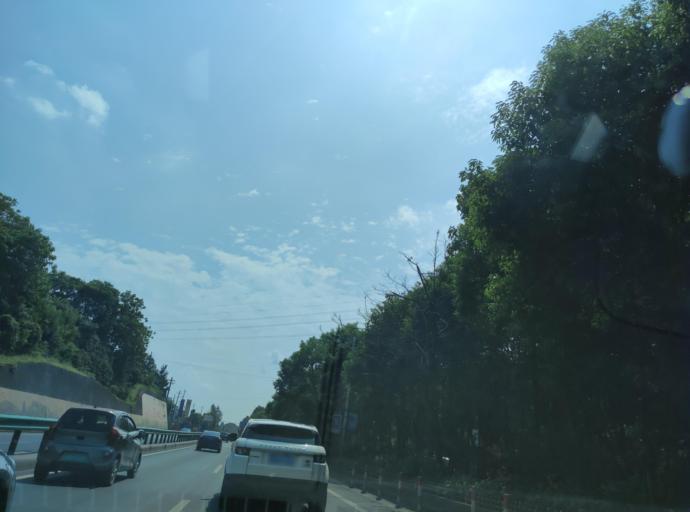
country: CN
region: Jiangxi Sheng
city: Pingxiang
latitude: 27.6511
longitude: 113.9199
